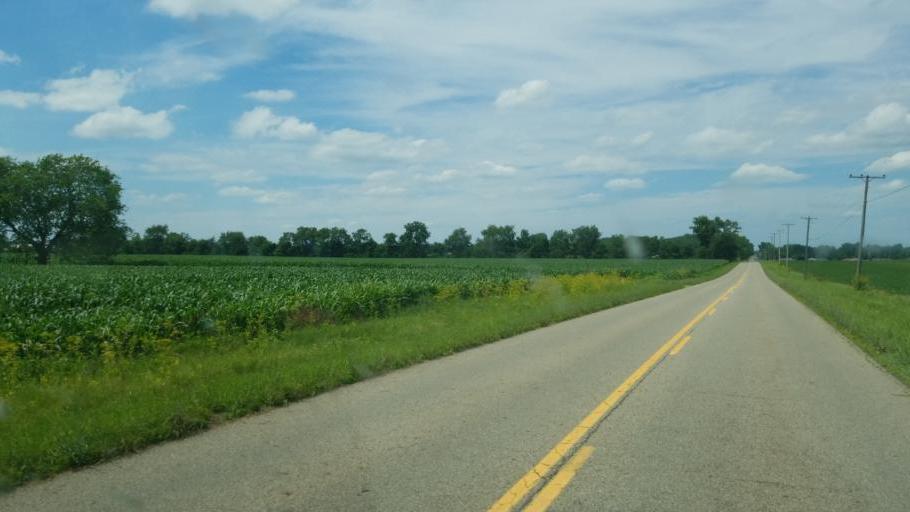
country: US
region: Ohio
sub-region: Knox County
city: Fredericktown
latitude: 40.4602
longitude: -82.5416
